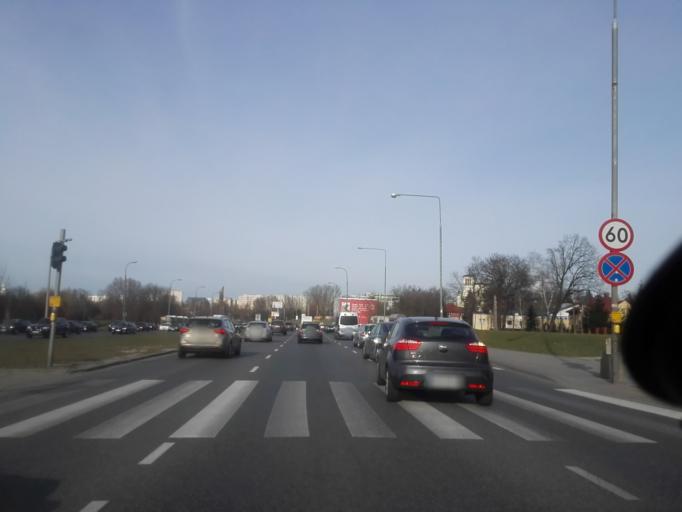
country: PL
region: Masovian Voivodeship
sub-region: Warszawa
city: Ursynow
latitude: 52.1704
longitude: 21.0411
